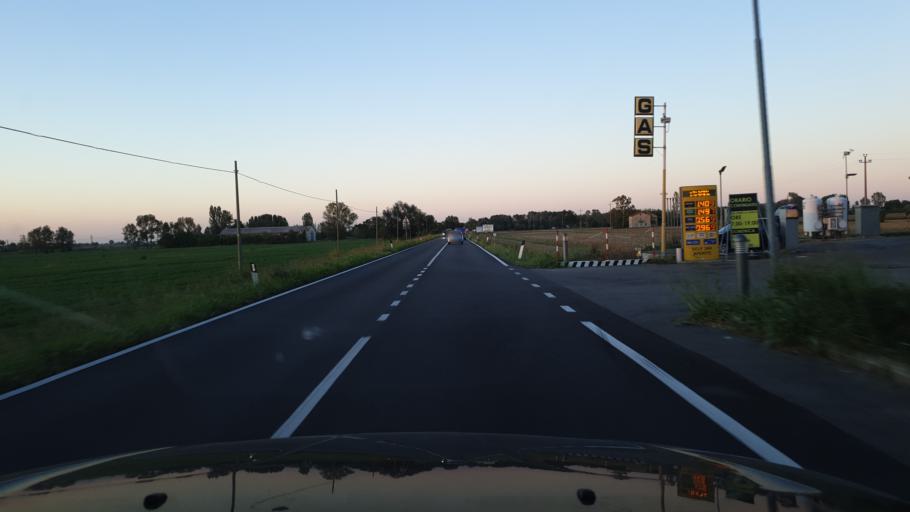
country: IT
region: Emilia-Romagna
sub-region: Provincia di Bologna
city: Granarolo dell'Emilia e Viadagola
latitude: 44.5893
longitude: 11.4312
